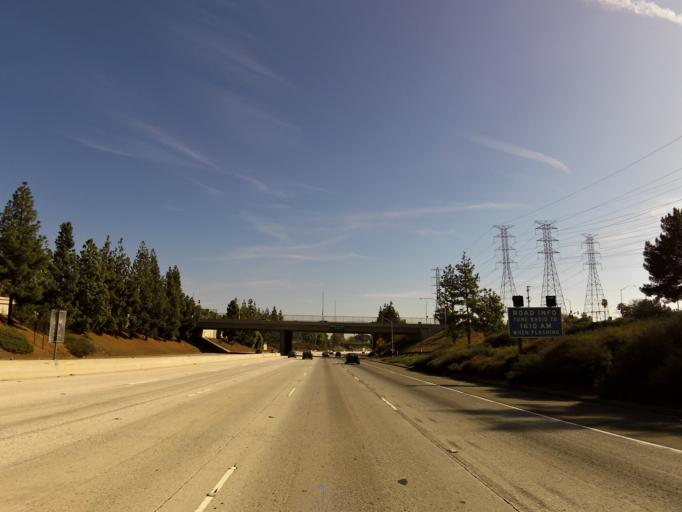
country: US
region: California
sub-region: Los Angeles County
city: Northridge
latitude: 34.2779
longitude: -118.5042
